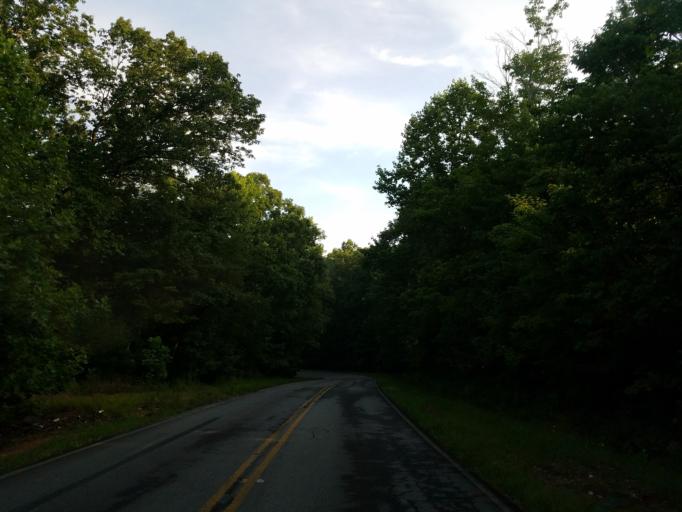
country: US
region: Georgia
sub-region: Pickens County
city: Jasper
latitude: 34.5382
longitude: -84.4407
